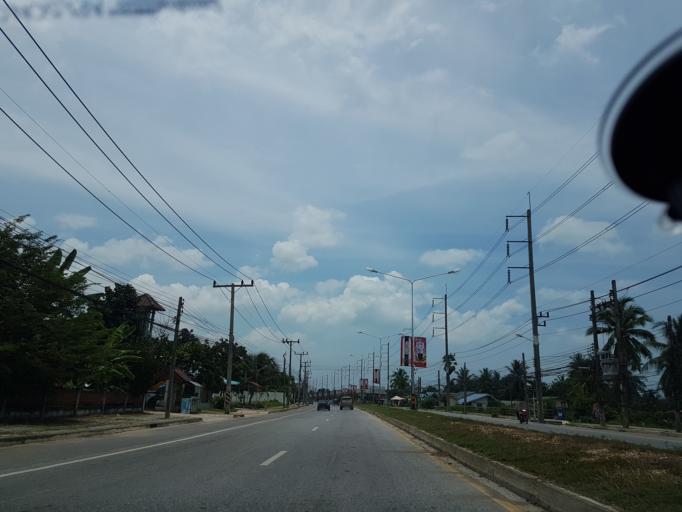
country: TH
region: Songkhla
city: Songkhla
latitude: 7.1102
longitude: 100.6328
